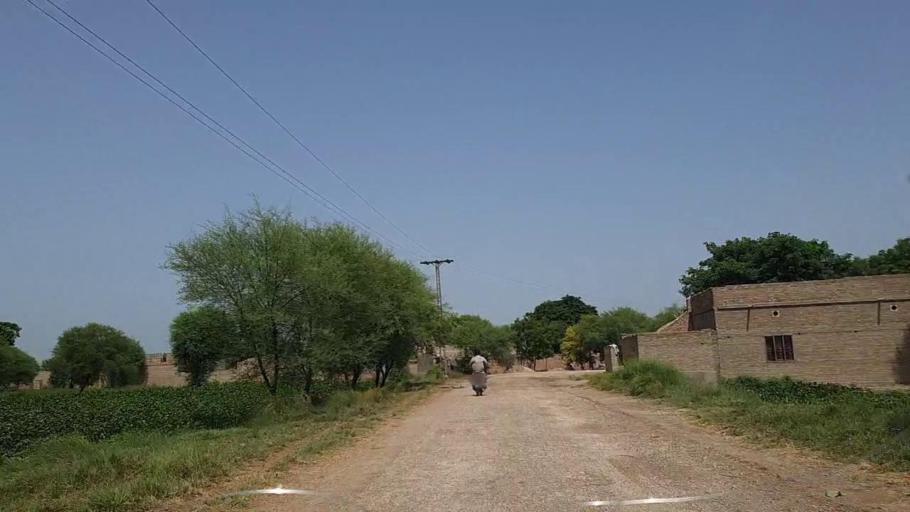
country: PK
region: Sindh
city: Kandiaro
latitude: 27.0150
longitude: 68.1555
